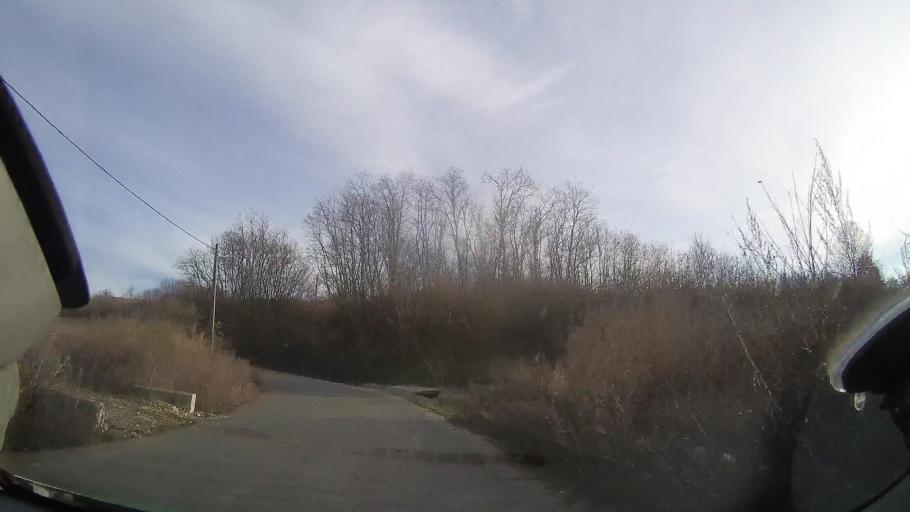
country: RO
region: Bihor
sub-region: Comuna Sarbi
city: Burzuc
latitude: 47.1363
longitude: 22.1843
